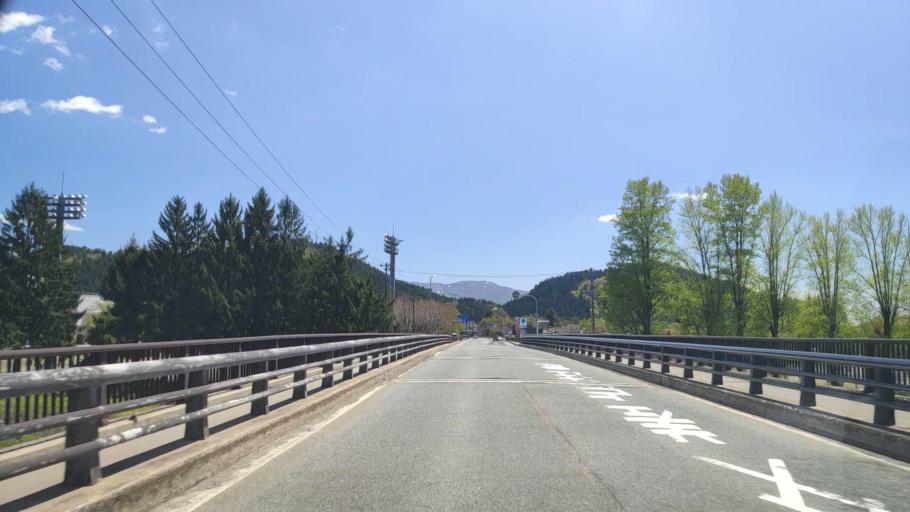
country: JP
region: Yamagata
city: Shinjo
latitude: 38.8857
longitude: 140.3345
